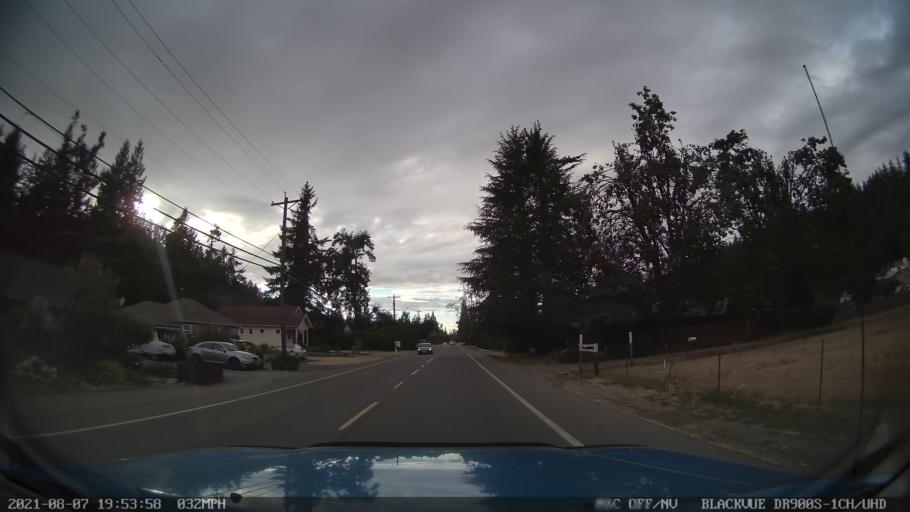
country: US
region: Oregon
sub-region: Marion County
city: Silverton
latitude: 44.9918
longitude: -122.7700
